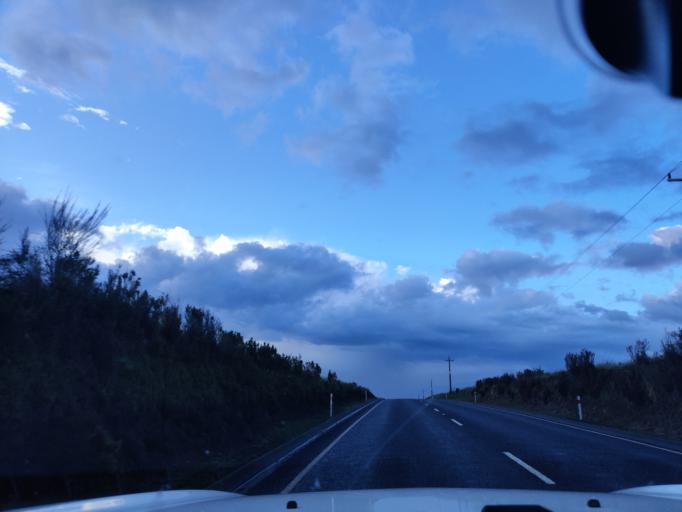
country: NZ
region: Waikato
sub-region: South Waikato District
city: Tokoroa
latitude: -38.3875
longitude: 175.7811
